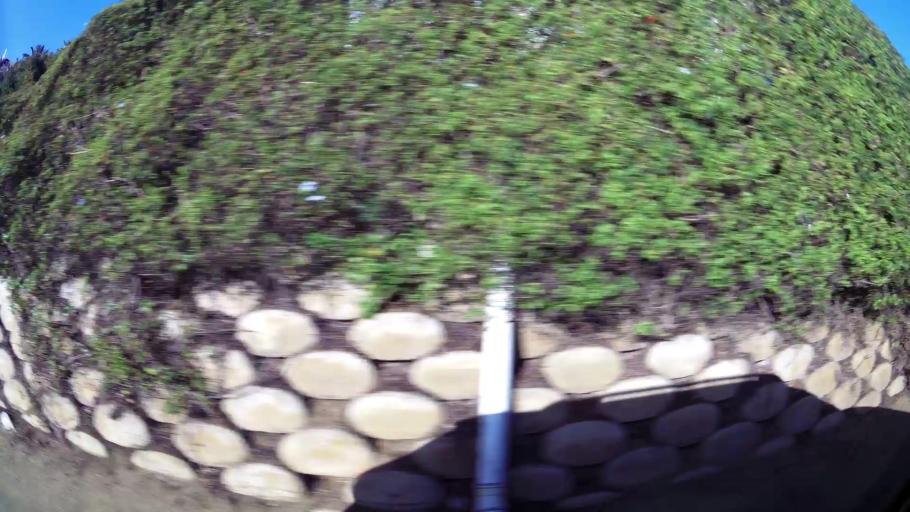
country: ZA
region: Western Cape
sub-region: Eden District Municipality
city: George
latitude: -33.9922
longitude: 22.5766
